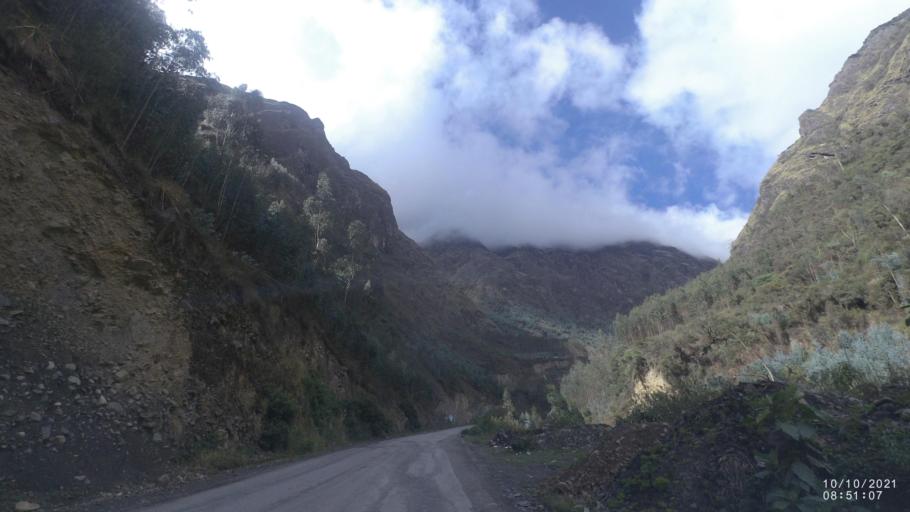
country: BO
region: La Paz
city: Quime
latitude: -16.9827
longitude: -67.2272
